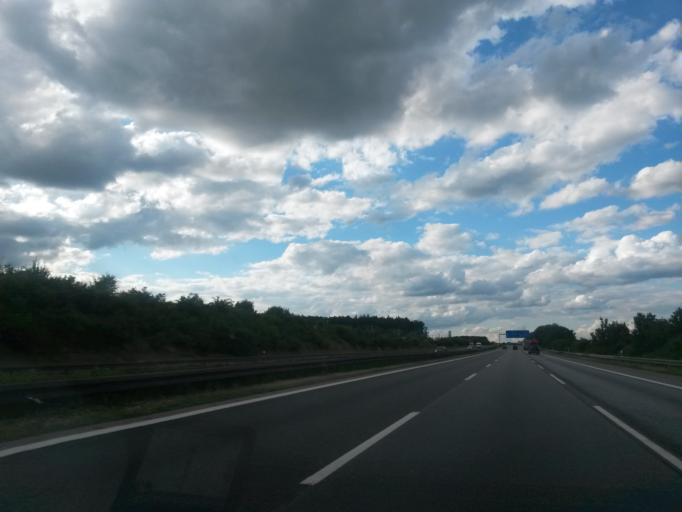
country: DE
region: Bavaria
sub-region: Regierungsbezirk Mittelfranken
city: Thalmassing
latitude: 49.1505
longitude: 11.2664
